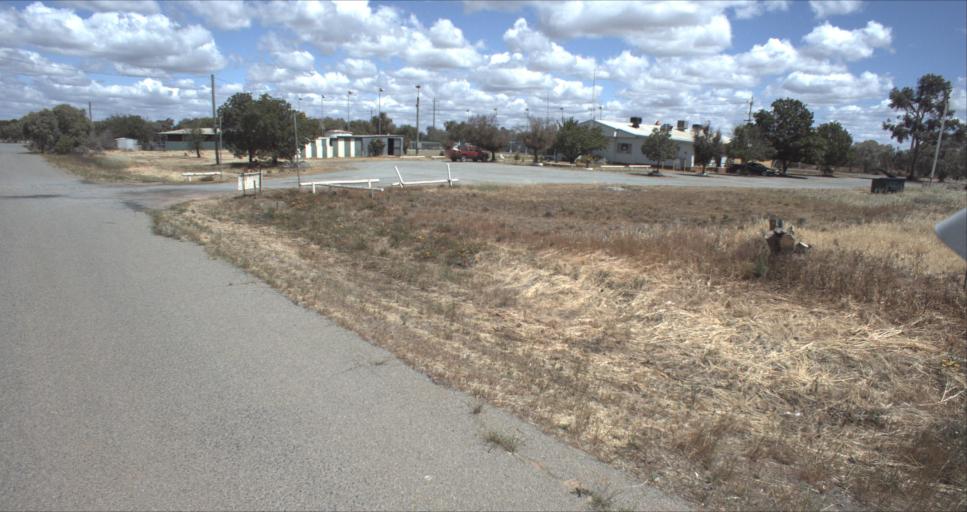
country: AU
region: New South Wales
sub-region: Murrumbidgee Shire
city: Darlington Point
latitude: -34.5157
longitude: 146.1779
